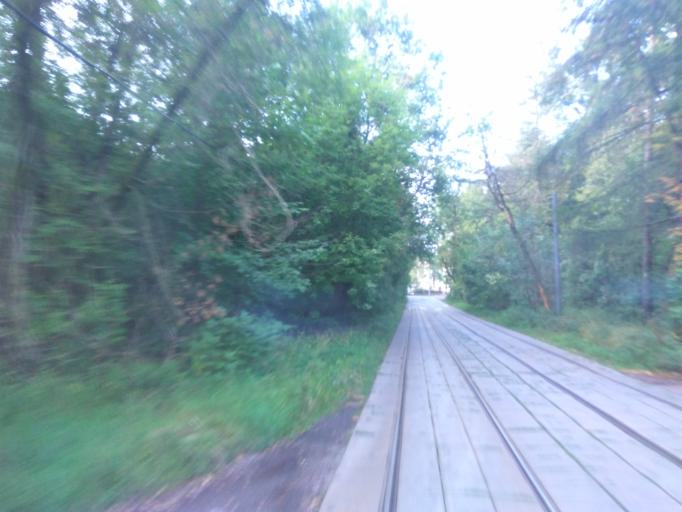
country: RU
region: Moscow
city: Sokol'niki
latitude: 55.8047
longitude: 37.6907
